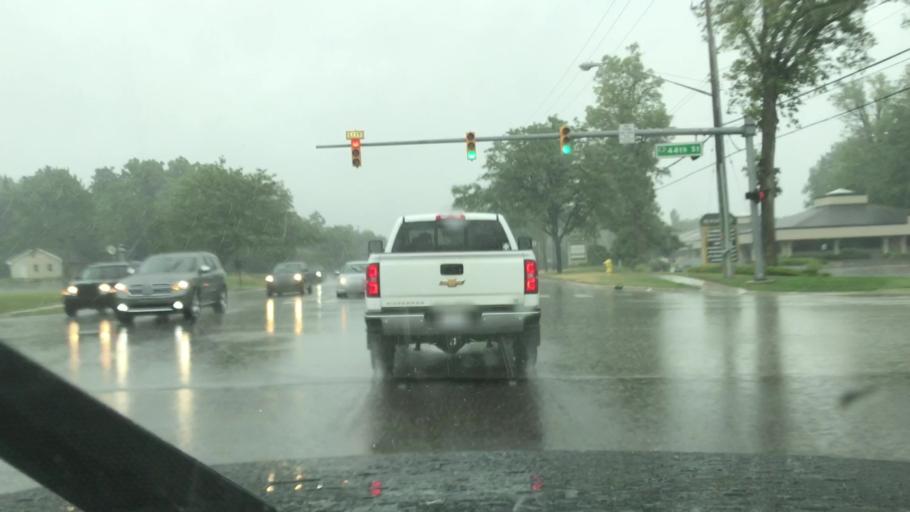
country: US
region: Michigan
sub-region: Kent County
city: Wyoming
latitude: 42.8849
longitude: -85.7242
